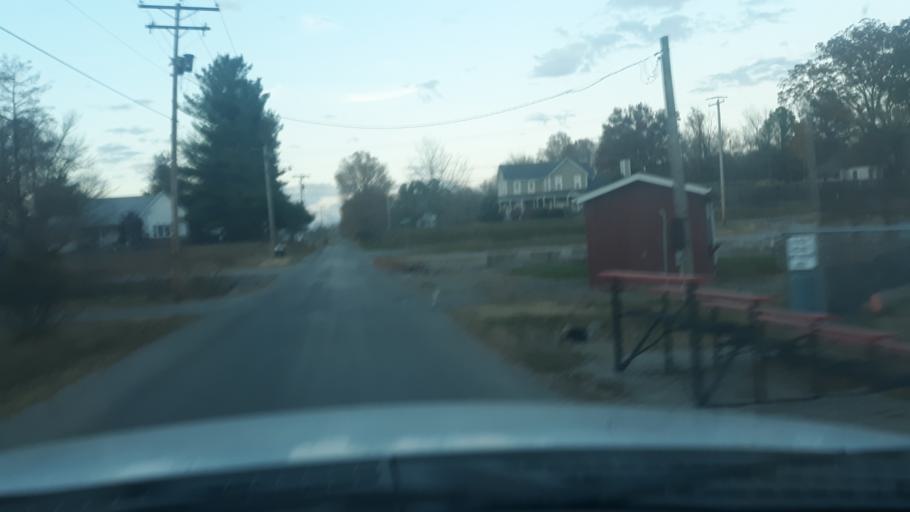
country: US
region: Illinois
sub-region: Saline County
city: Harrisburg
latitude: 37.8425
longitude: -88.6145
